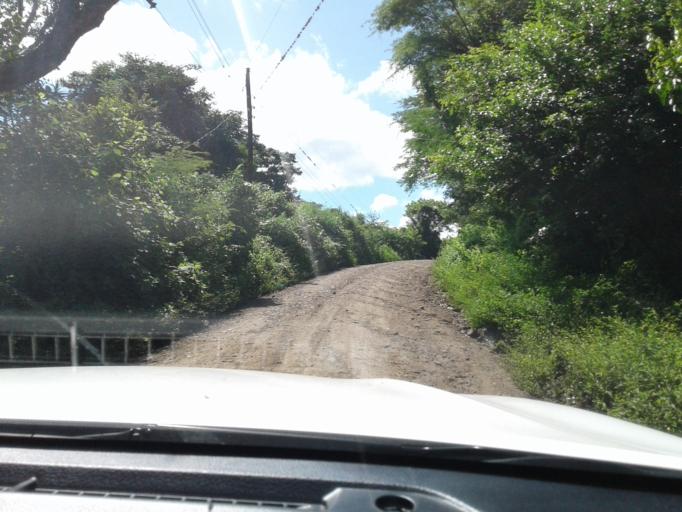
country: NI
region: Matagalpa
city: Terrabona
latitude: 12.8432
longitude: -86.0057
